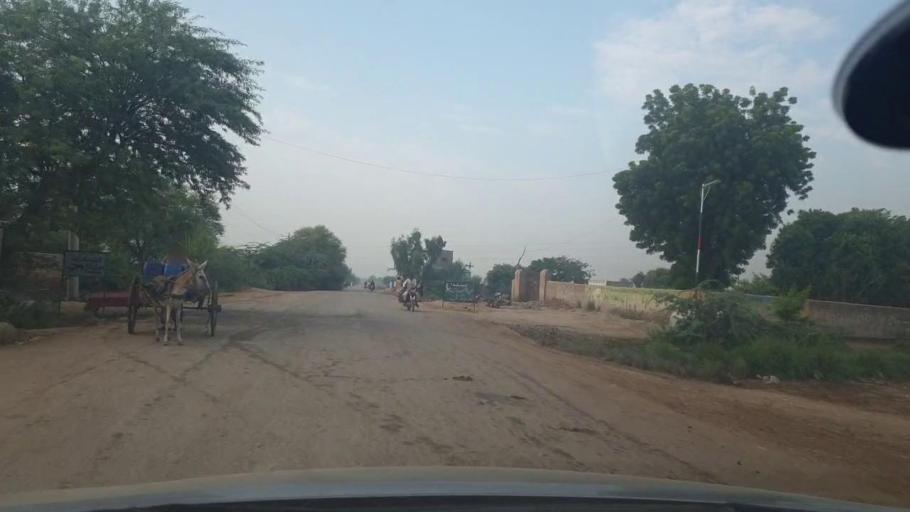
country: PK
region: Sindh
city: Jacobabad
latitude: 28.2740
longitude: 68.4224
